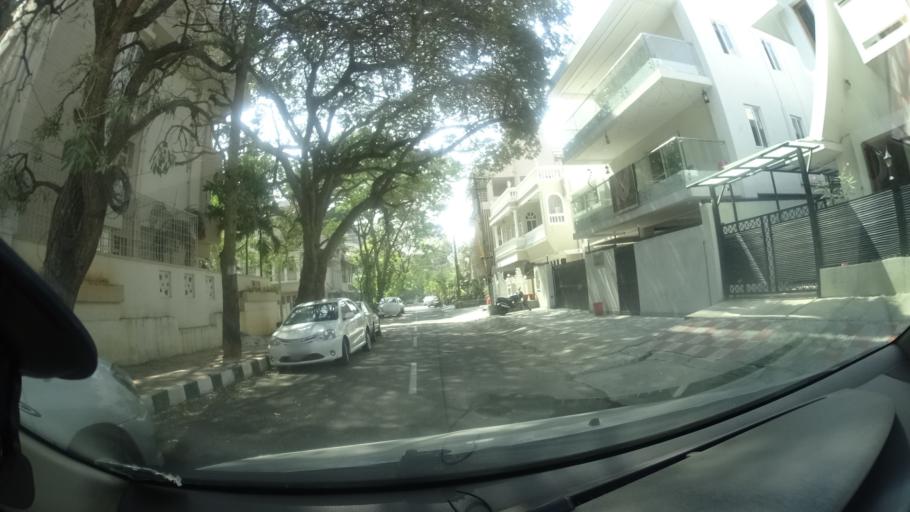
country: IN
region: Karnataka
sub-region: Bangalore Urban
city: Bangalore
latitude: 13.0129
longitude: 77.5765
